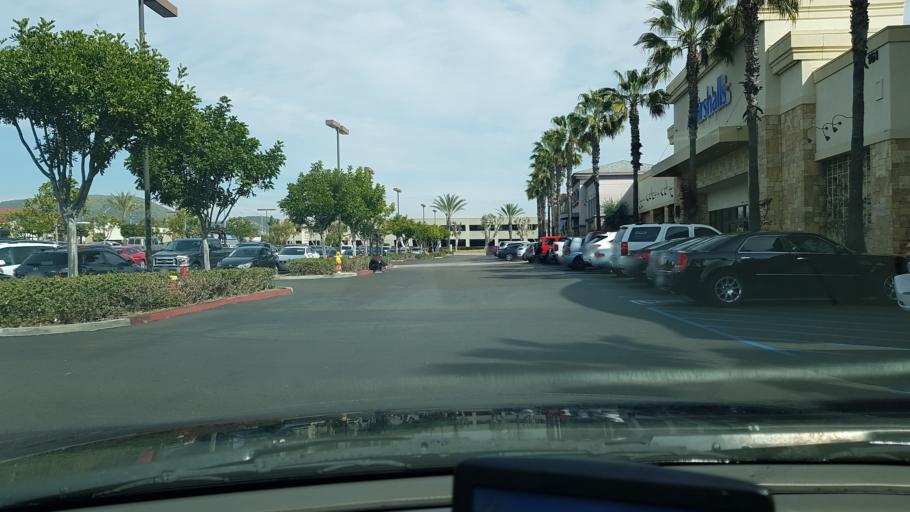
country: US
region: California
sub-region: San Diego County
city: Lake San Marcos
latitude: 33.1392
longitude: -117.1914
